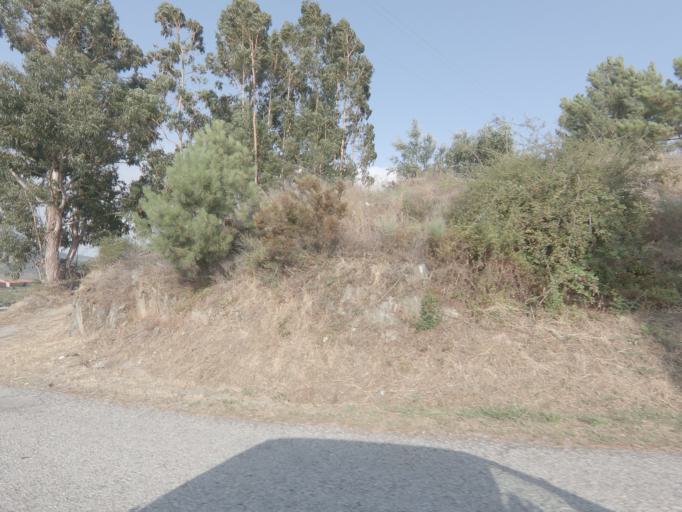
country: PT
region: Viseu
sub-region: Tabuaco
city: Tabuaco
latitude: 41.1615
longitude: -7.5605
